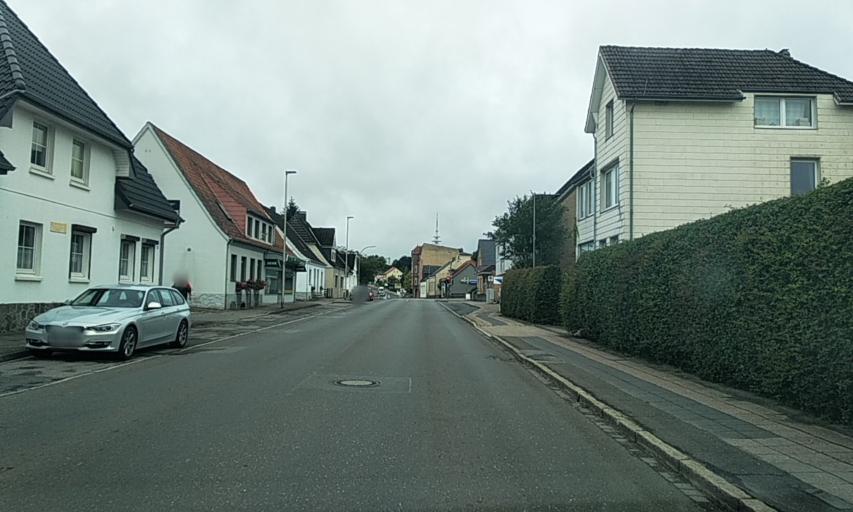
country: DE
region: Schleswig-Holstein
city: Schleswig
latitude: 54.5227
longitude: 9.5473
